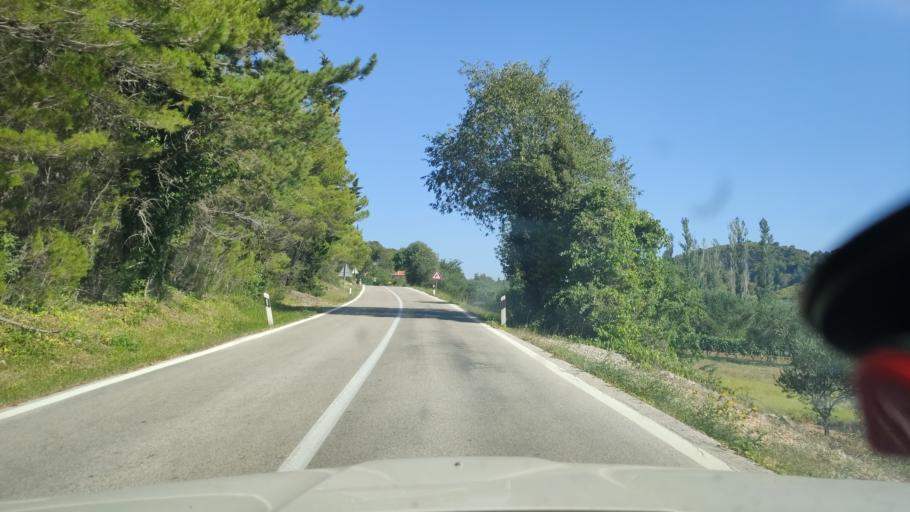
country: HR
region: Sibensko-Kniniska
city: Zaton
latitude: 43.8536
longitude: 15.8972
